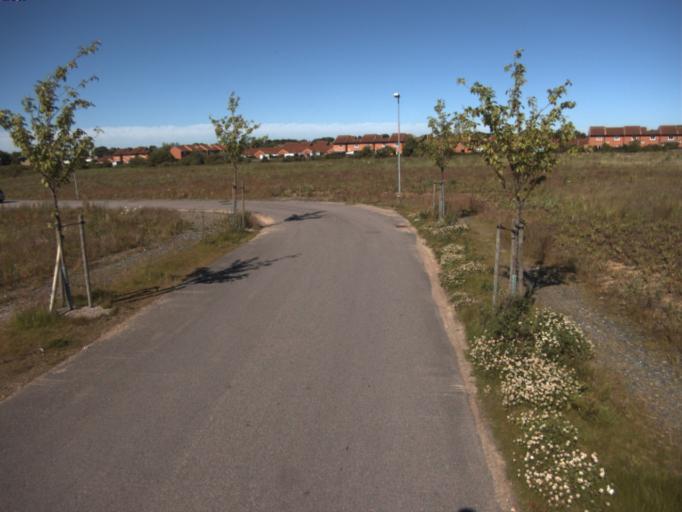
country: SE
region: Skane
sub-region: Helsingborg
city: Odakra
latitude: 56.0943
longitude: 12.7463
